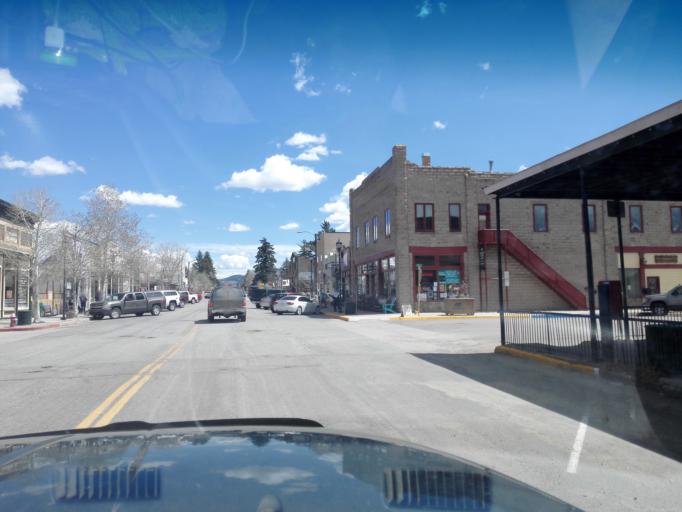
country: US
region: Colorado
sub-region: Custer County
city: Westcliffe
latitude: 38.1361
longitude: -105.4689
